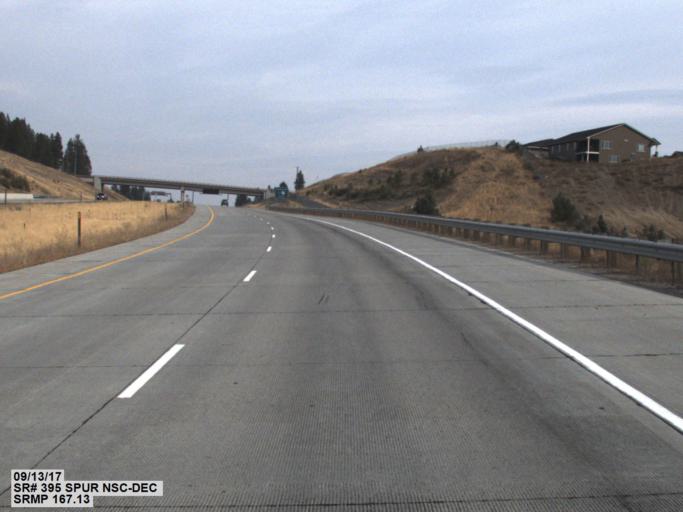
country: US
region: Washington
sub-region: Spokane County
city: Fairwood
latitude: 47.7787
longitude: -117.3970
